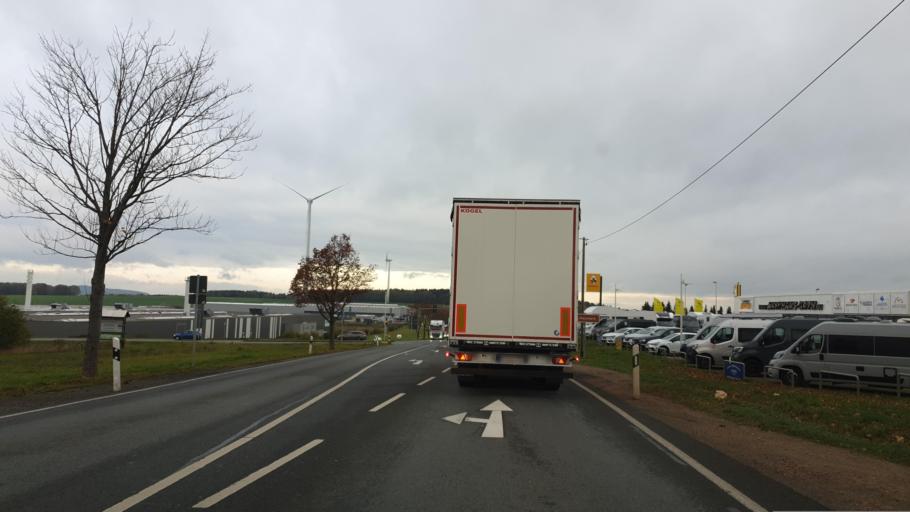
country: DE
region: Saxony
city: Reichenbach/Vogtland
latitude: 50.5988
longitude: 12.3284
